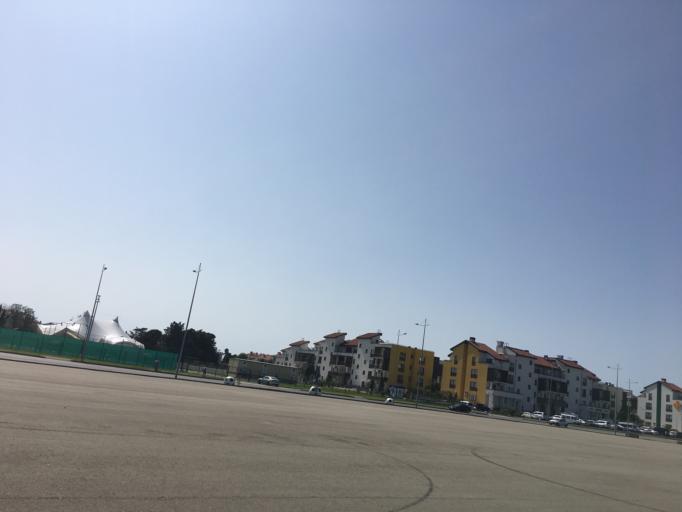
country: RU
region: Krasnodarskiy
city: Adler
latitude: 43.4119
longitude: 39.9454
